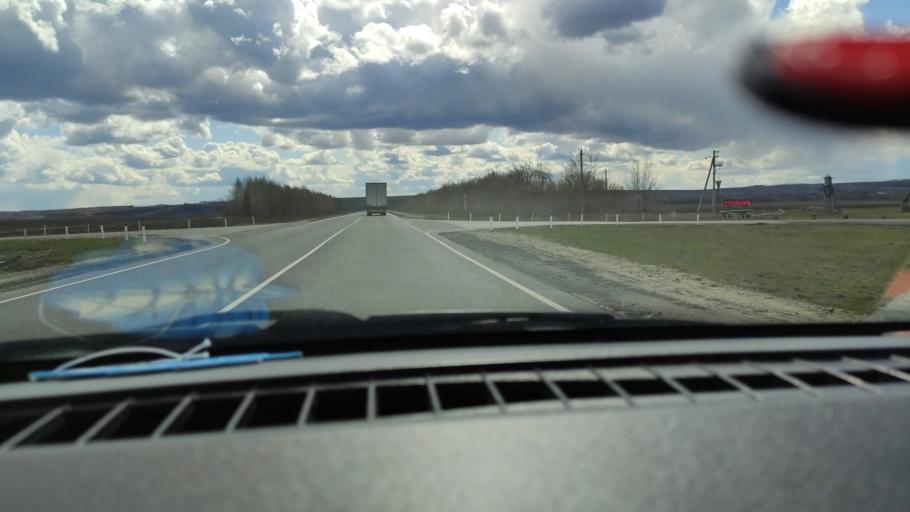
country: RU
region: Samara
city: Syzran'
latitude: 52.9826
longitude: 48.3145
